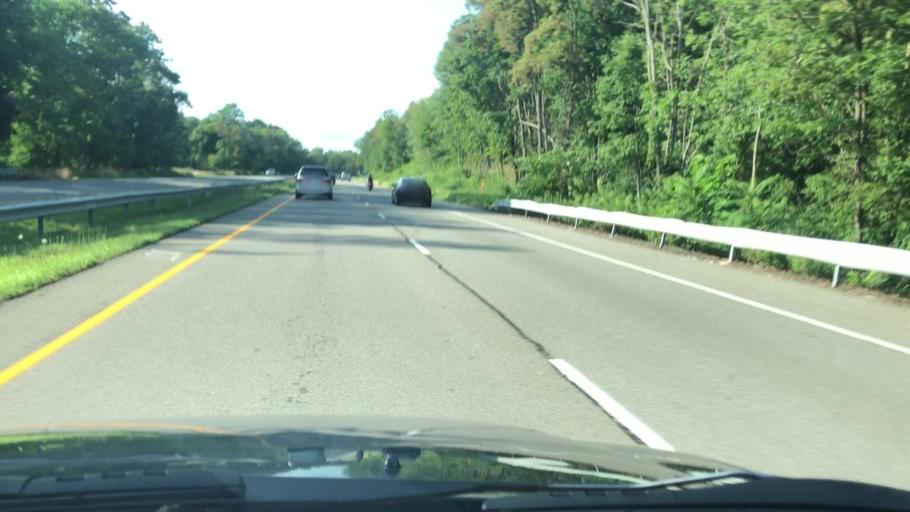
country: US
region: New York
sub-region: Dutchess County
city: Fishkill
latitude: 41.5496
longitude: -73.9039
